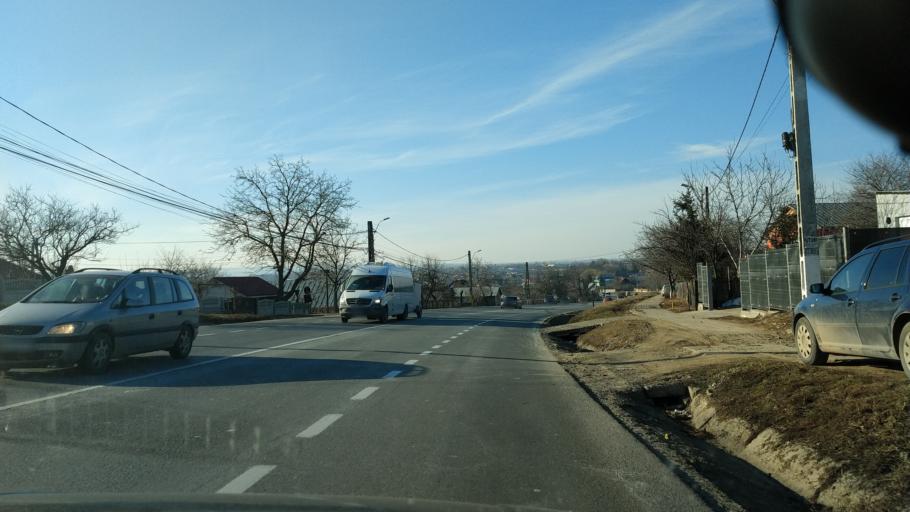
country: RO
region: Iasi
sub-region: Comuna Ion Neculce
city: Razboieni
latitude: 47.2175
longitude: 27.0427
